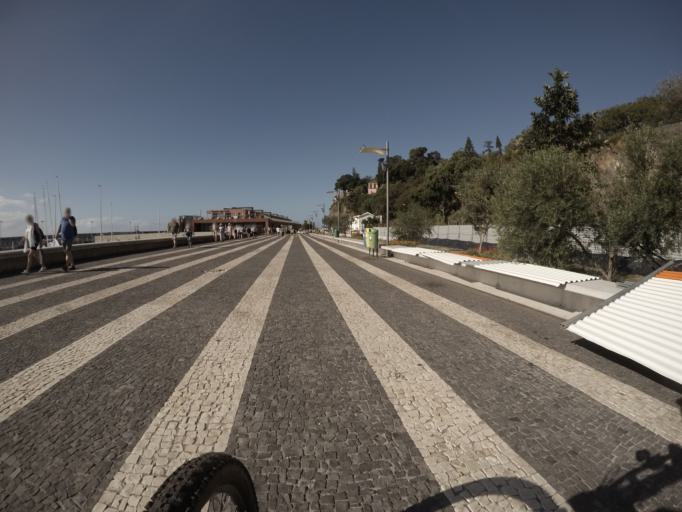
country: PT
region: Madeira
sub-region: Funchal
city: Funchal
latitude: 32.6448
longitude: -16.9134
